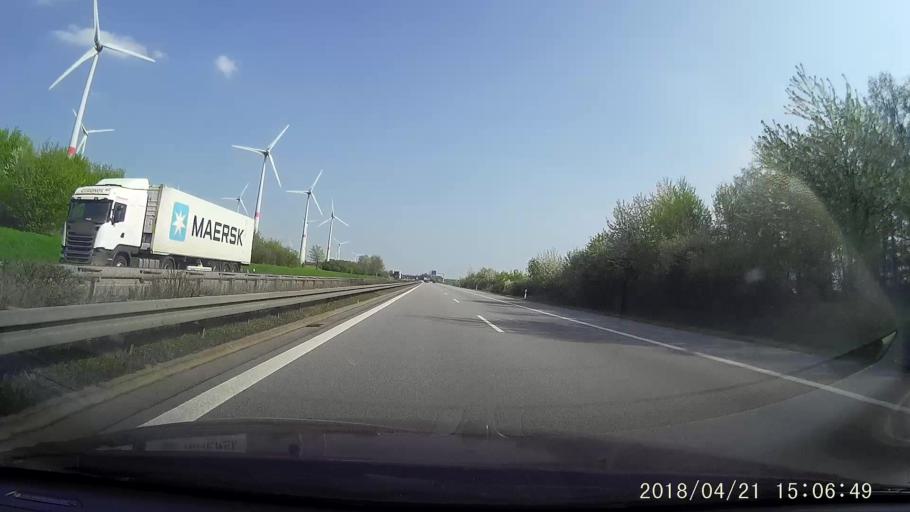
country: DE
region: Saxony
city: Kodersdorf
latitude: 51.2075
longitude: 14.9452
